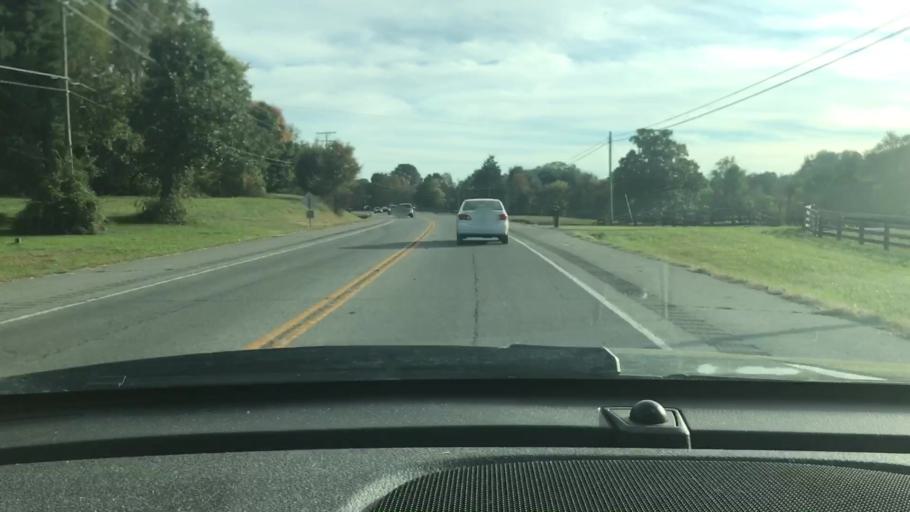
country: US
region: Tennessee
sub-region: Sumner County
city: Millersville
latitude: 36.4223
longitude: -86.6949
